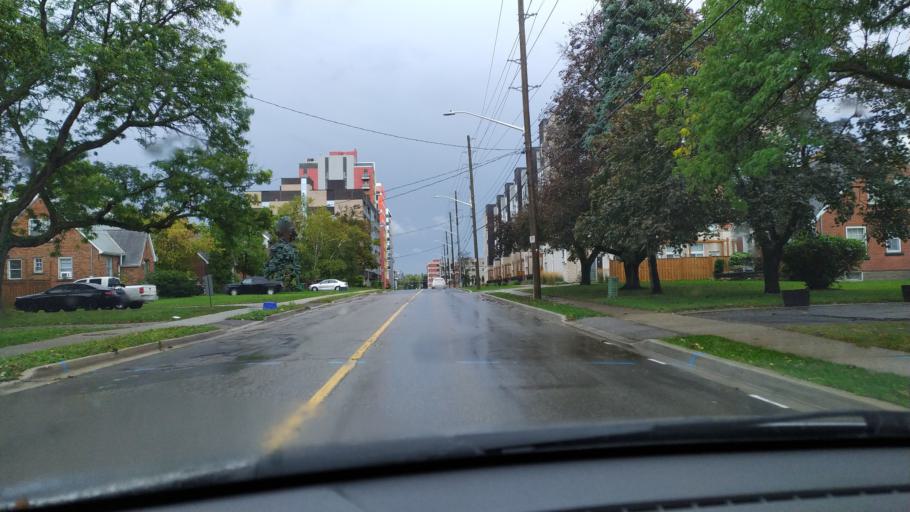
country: CA
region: Ontario
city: Waterloo
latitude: 43.4764
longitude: -80.5336
